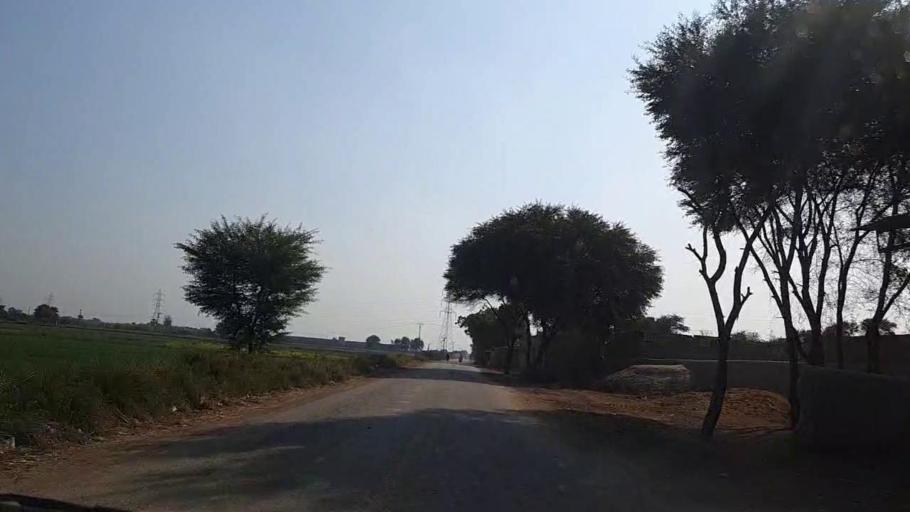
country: PK
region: Sindh
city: Sakrand
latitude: 26.1099
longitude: 68.2909
